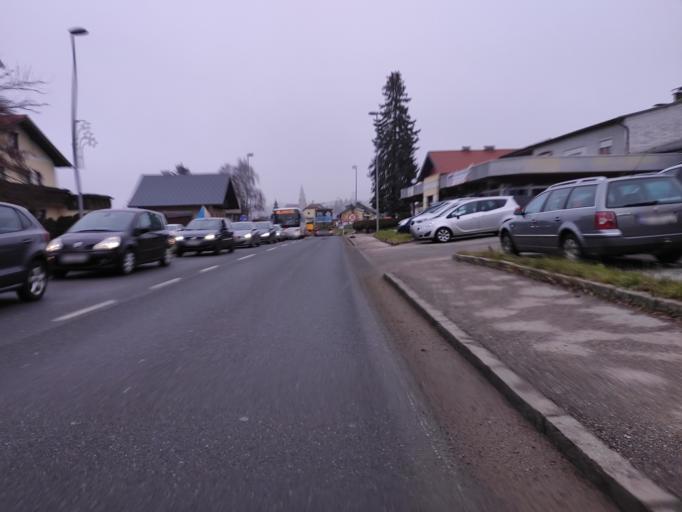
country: AT
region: Salzburg
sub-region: Politischer Bezirk Salzburg-Umgebung
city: Strasswalchen
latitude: 47.9747
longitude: 13.2517
